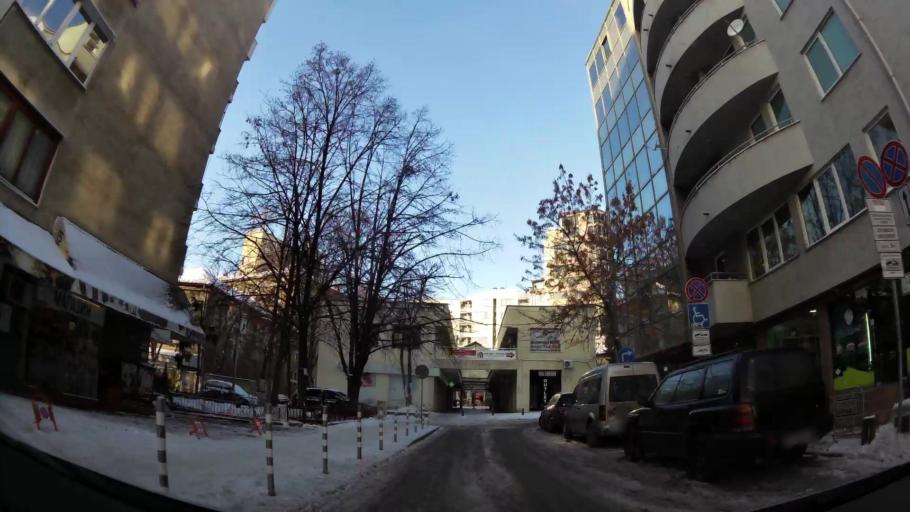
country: BG
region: Sofia-Capital
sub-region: Stolichna Obshtina
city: Sofia
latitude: 42.6706
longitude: 23.3215
